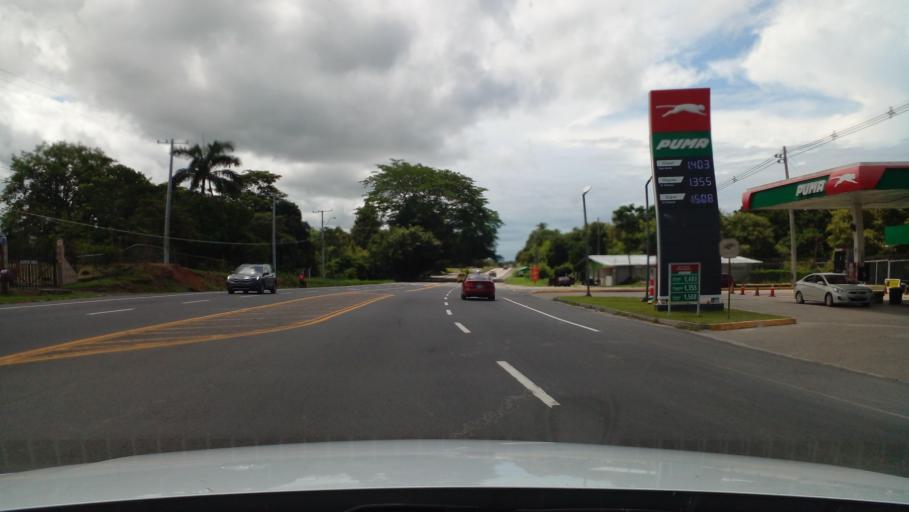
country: PA
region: Panama
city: Las Colinas
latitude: 8.4367
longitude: -80.0588
